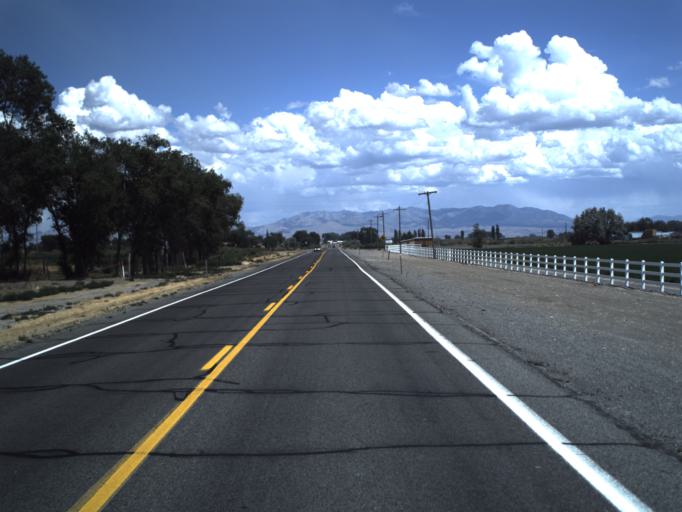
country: US
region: Utah
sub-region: Millard County
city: Delta
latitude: 39.3305
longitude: -112.6286
